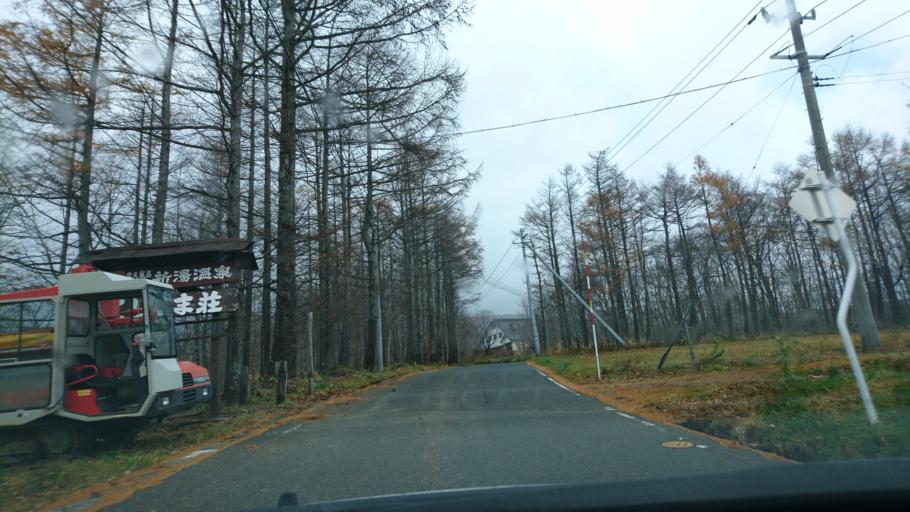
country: JP
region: Iwate
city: Ichinoseki
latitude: 38.9298
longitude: 140.8382
